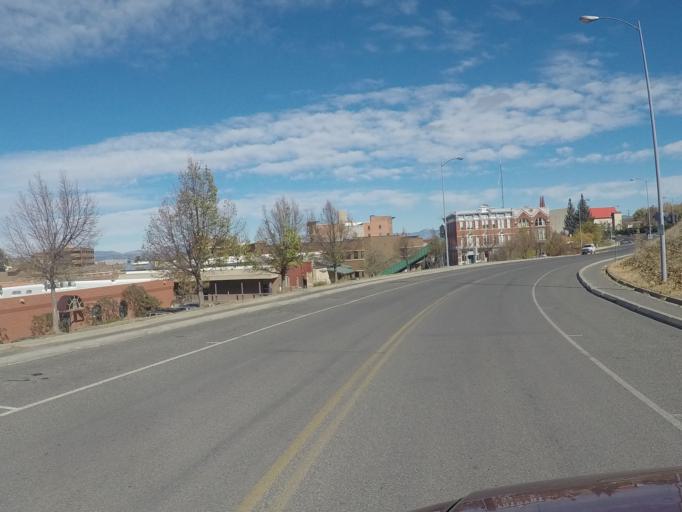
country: US
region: Montana
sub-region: Lewis and Clark County
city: Helena
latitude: 46.5852
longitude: -112.0402
